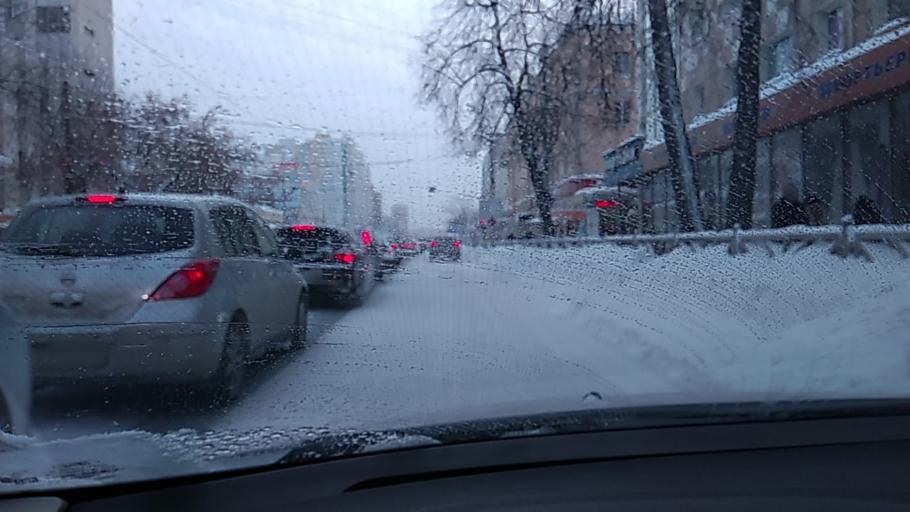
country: RU
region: Sverdlovsk
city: Yekaterinburg
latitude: 56.8096
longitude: 60.6096
